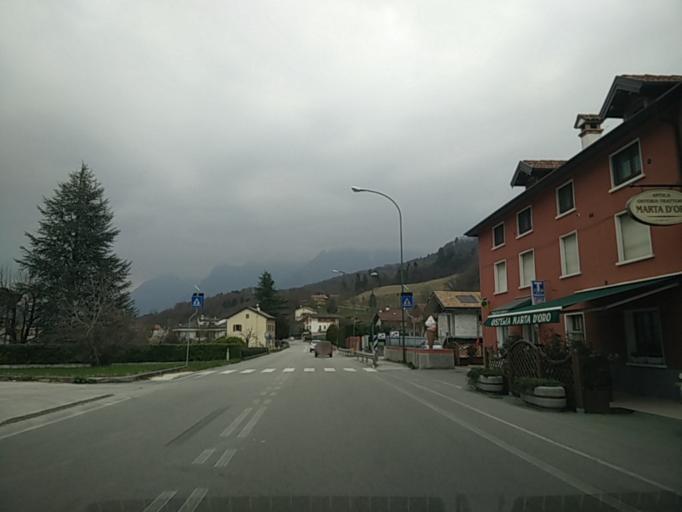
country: IT
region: Veneto
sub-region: Provincia di Belluno
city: Ponte nell'Alpi
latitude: 46.1526
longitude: 12.2630
